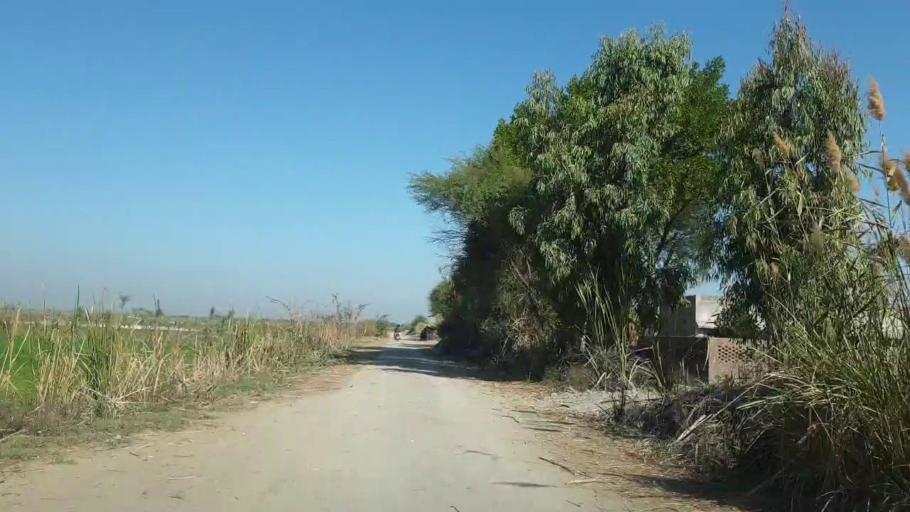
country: PK
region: Sindh
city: Mirpur Khas
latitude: 25.6198
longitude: 69.0238
